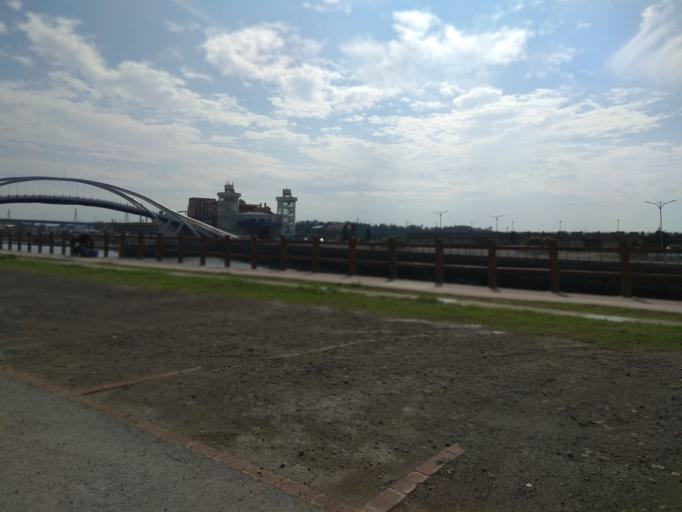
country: TW
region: Taiwan
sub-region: Hsinchu
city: Zhubei
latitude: 24.9894
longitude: 121.0131
